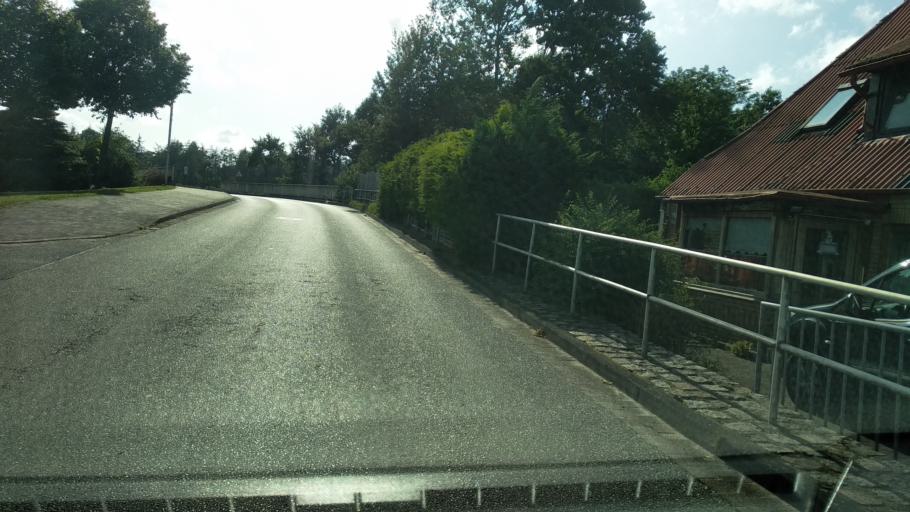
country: DE
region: Schleswig-Holstein
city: Busdorf
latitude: 54.4905
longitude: 9.5500
